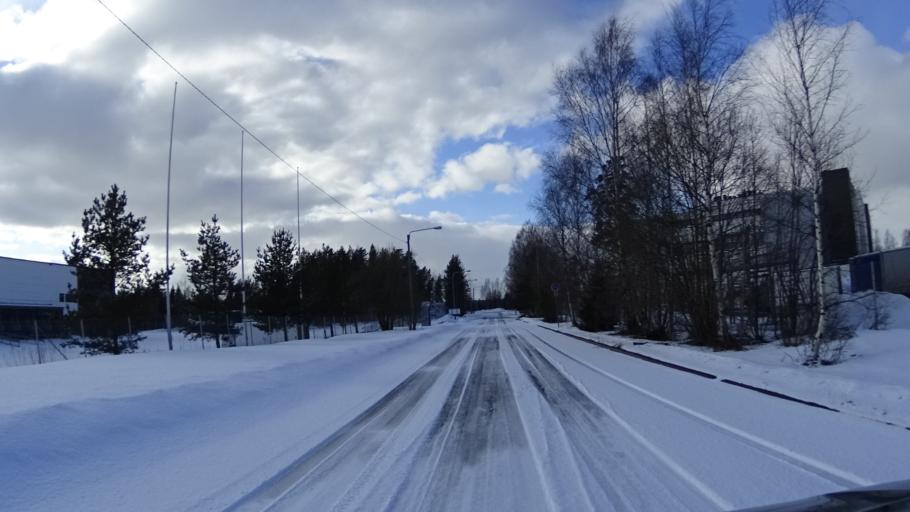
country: FI
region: Uusimaa
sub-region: Helsinki
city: Vantaa
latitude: 60.2979
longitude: 25.0903
